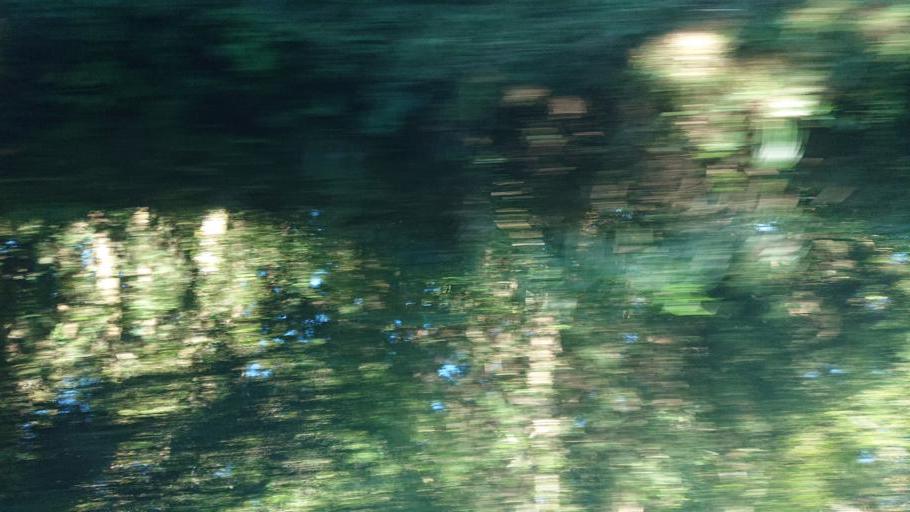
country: TW
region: Taiwan
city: Lugu
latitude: 23.4949
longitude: 120.7940
